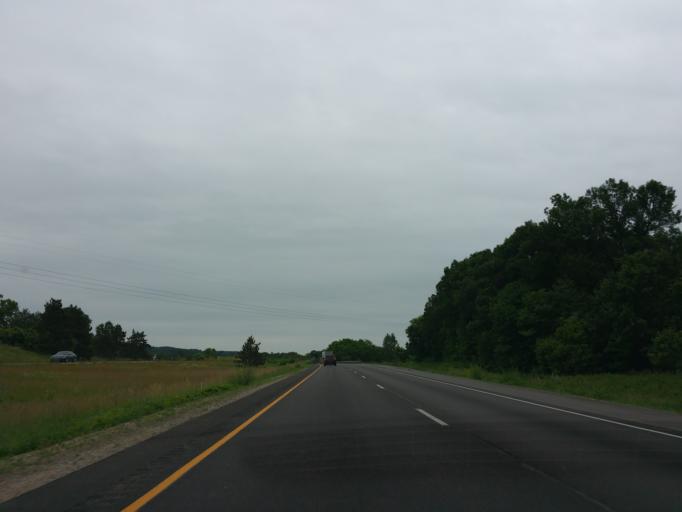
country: US
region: Wisconsin
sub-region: Eau Claire County
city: Fall Creek
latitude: 44.7336
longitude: -91.3679
